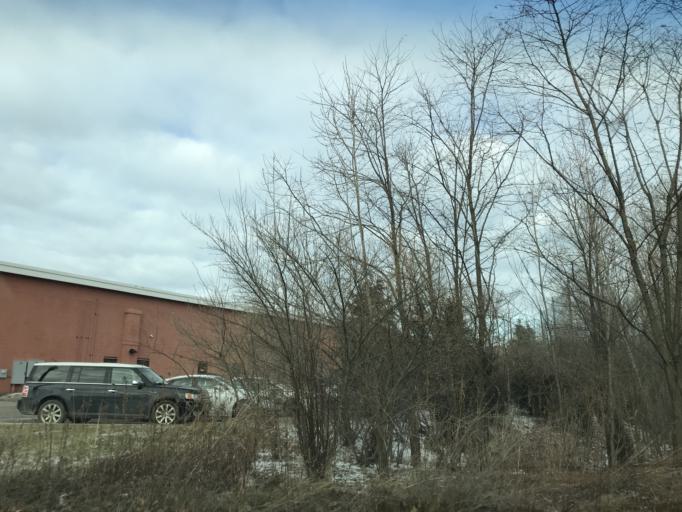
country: US
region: Michigan
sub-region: Oakland County
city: Clarkston
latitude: 42.7410
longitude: -83.3782
